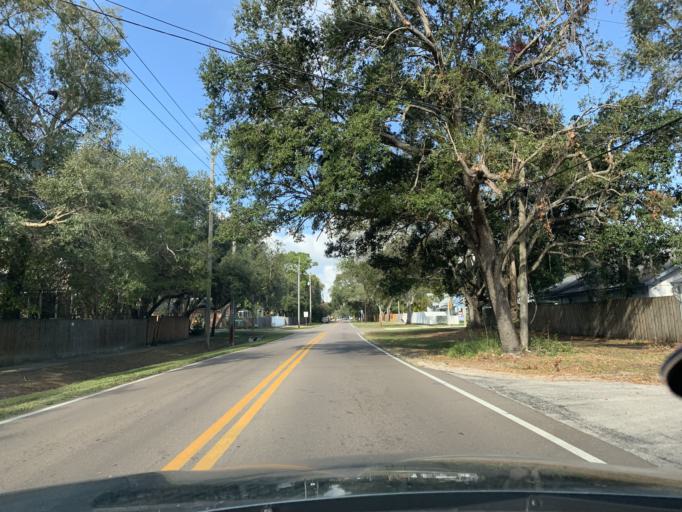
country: US
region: Florida
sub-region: Pinellas County
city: South Highpoint
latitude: 27.9051
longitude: -82.7127
